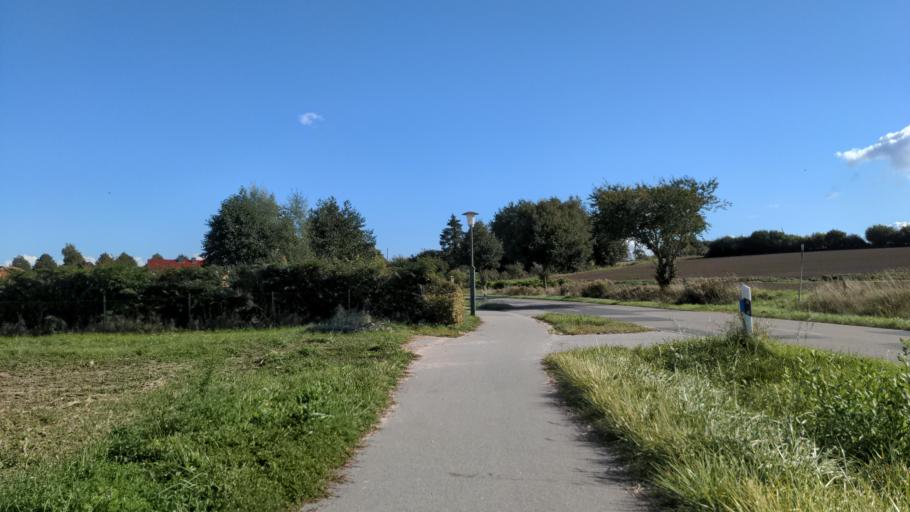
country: DE
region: Schleswig-Holstein
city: Schashagen
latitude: 54.1616
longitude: 10.9054
